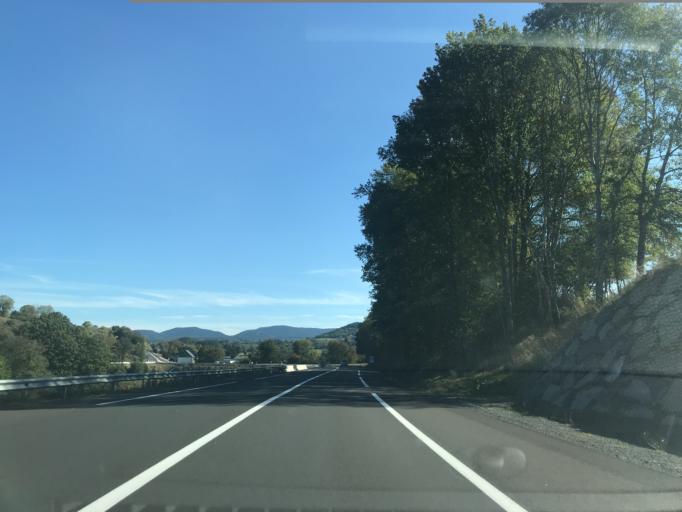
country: FR
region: Auvergne
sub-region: Departement du Puy-de-Dome
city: Gelles
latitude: 45.7315
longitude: 2.8260
